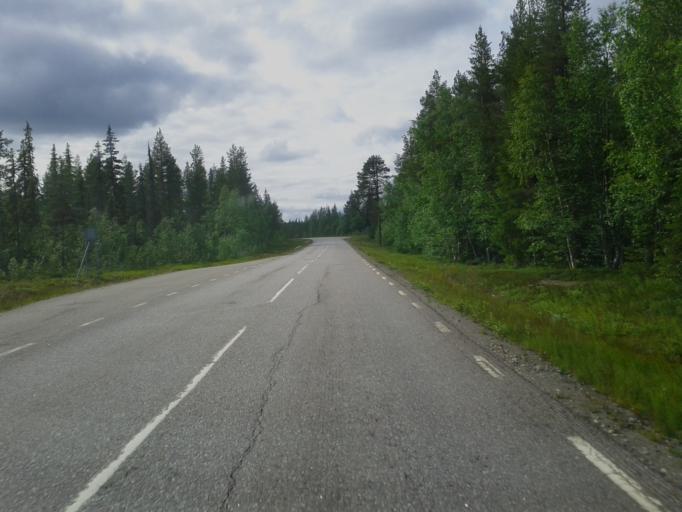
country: SE
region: Vaesterbotten
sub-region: Sorsele Kommun
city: Sorsele
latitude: 65.2860
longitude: 17.8466
